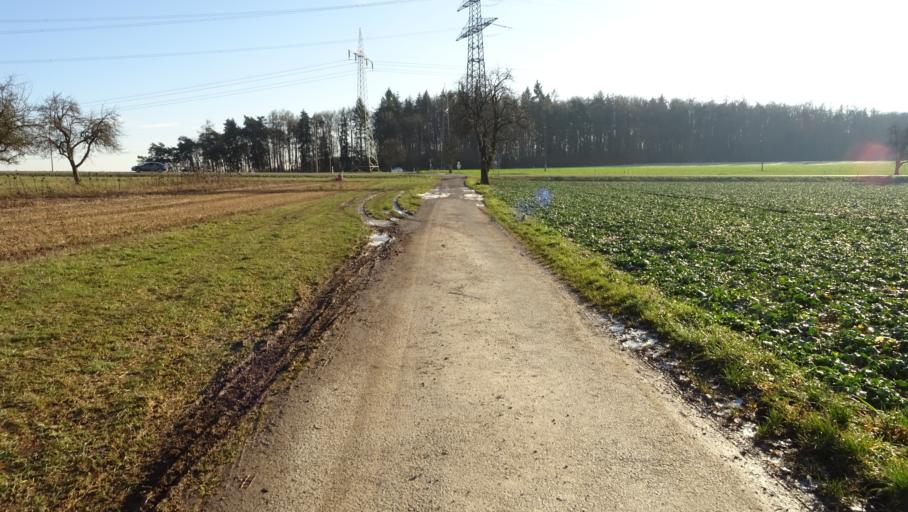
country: DE
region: Baden-Wuerttemberg
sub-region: Karlsruhe Region
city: Mosbach
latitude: 49.3449
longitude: 9.1960
